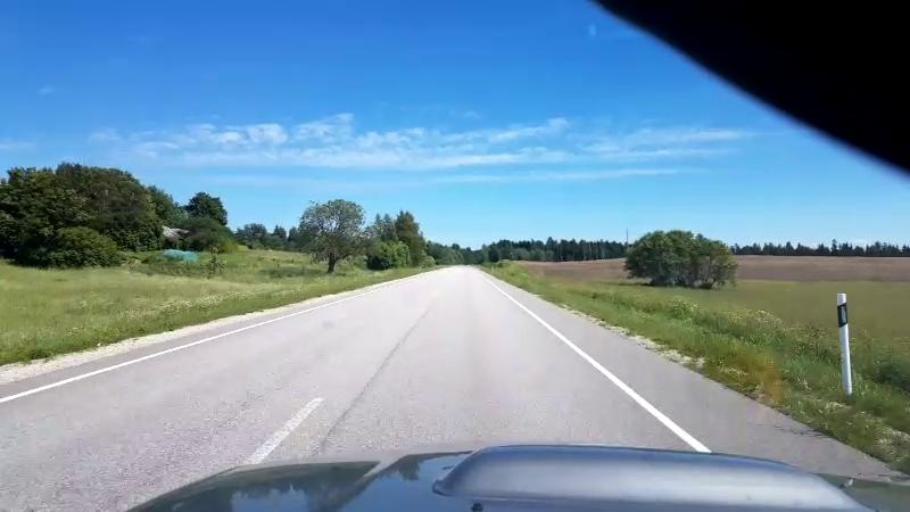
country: EE
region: Jaervamaa
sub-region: Koeru vald
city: Koeru
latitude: 58.9774
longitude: 26.0999
